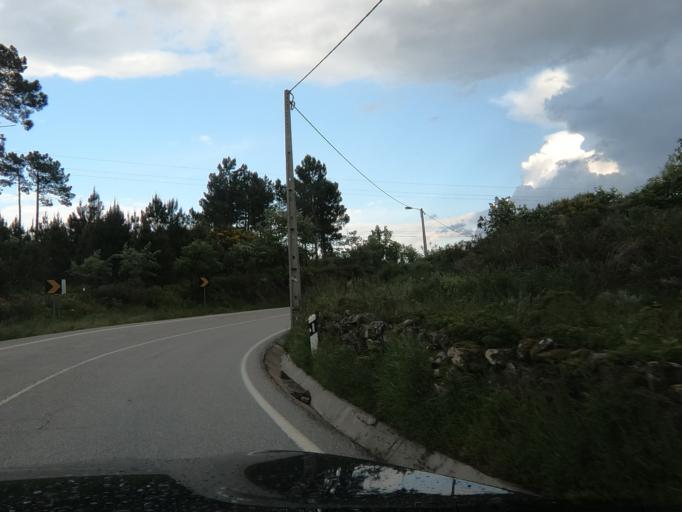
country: PT
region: Vila Real
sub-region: Vila Real
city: Vila Real
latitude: 41.3755
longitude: -7.7176
